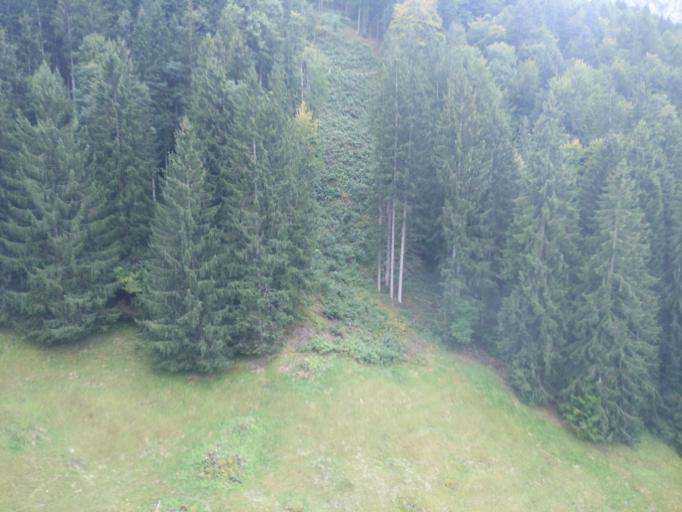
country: DE
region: Bavaria
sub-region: Upper Bavaria
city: Grainau
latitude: 47.4688
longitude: 11.0607
